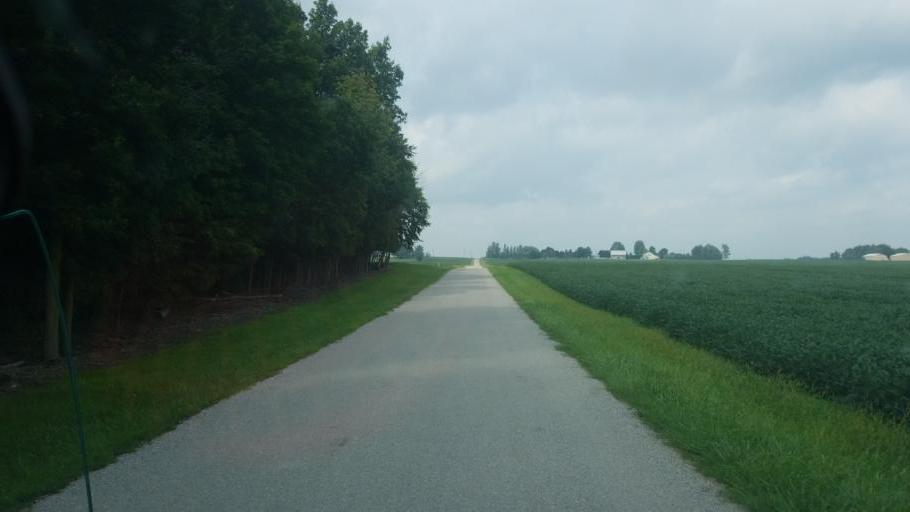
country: US
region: Ohio
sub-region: Huron County
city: New London
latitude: 41.0823
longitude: -82.4620
